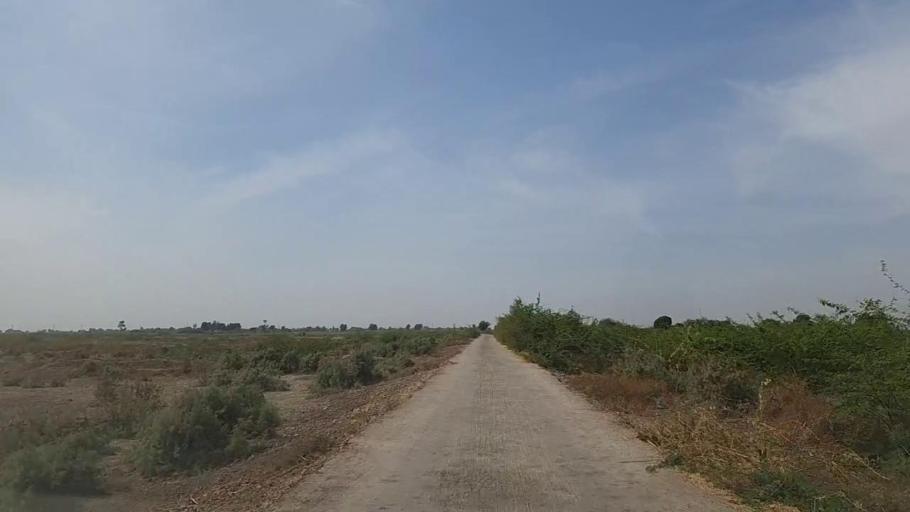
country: PK
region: Sindh
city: Kunri
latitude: 25.2129
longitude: 69.4756
